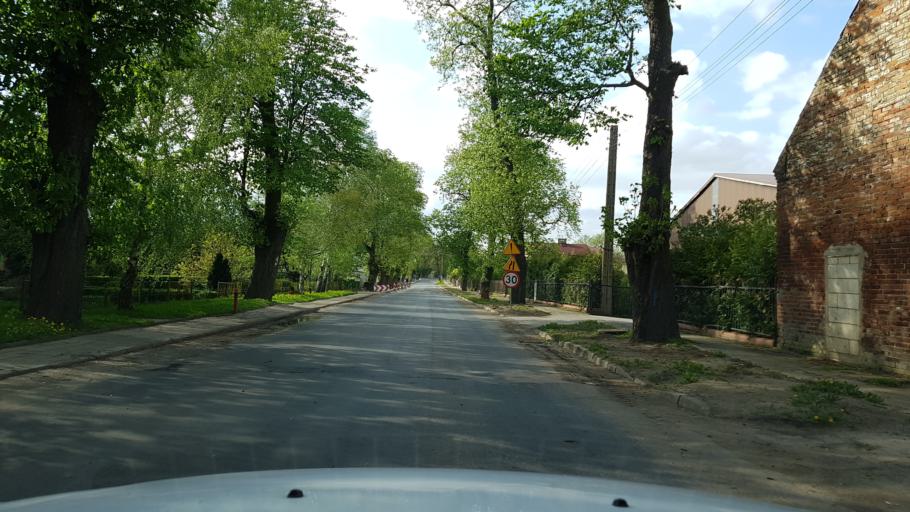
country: PL
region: West Pomeranian Voivodeship
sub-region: Powiat pyrzycki
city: Przelewice
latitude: 53.1012
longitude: 15.0826
